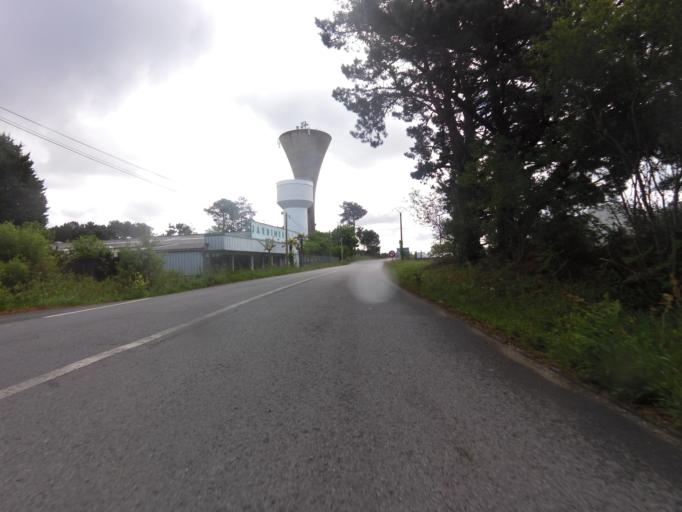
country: FR
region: Brittany
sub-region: Departement du Morbihan
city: Plougoumelen
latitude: 47.6667
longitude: -2.8980
